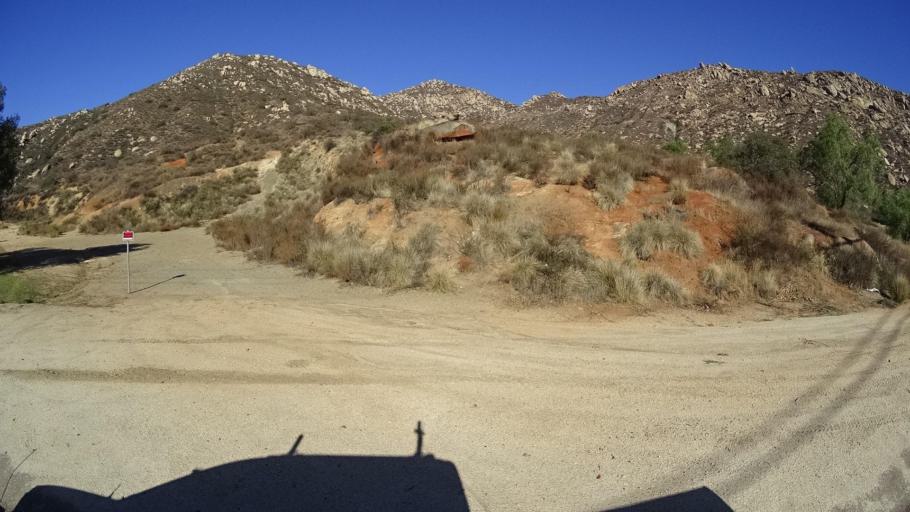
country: MX
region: Baja California
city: Tecate
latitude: 32.6207
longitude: -116.6933
